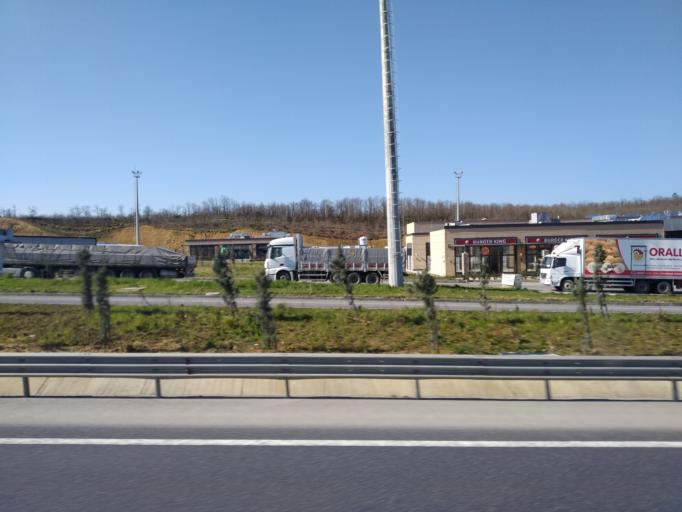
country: TR
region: Istanbul
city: Mahmut Sevket Pasa
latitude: 41.1020
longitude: 29.2915
